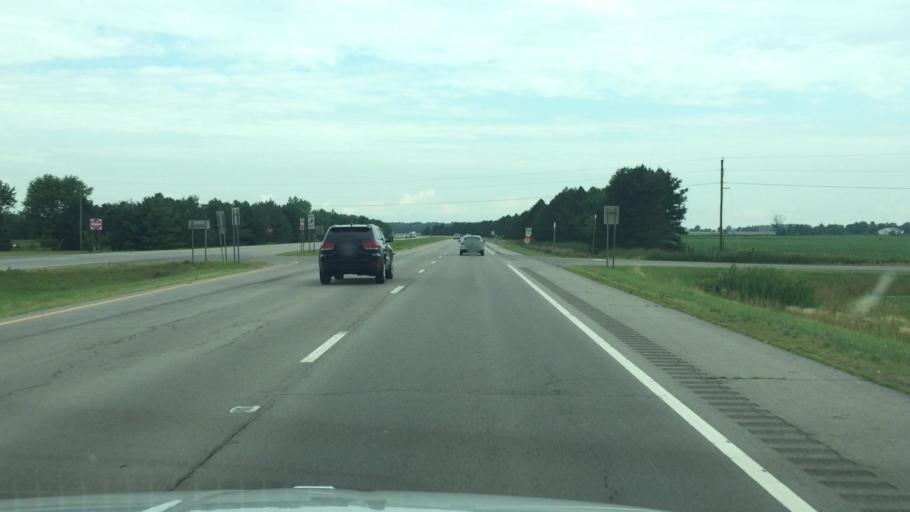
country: US
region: Ohio
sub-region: Wyandot County
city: Carey
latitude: 40.9753
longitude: -83.4904
